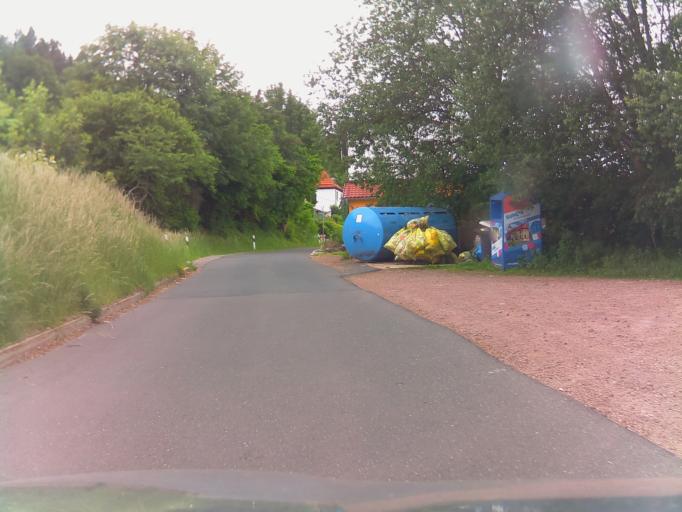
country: DE
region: Thuringia
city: Suhl
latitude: 50.6178
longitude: 10.6935
